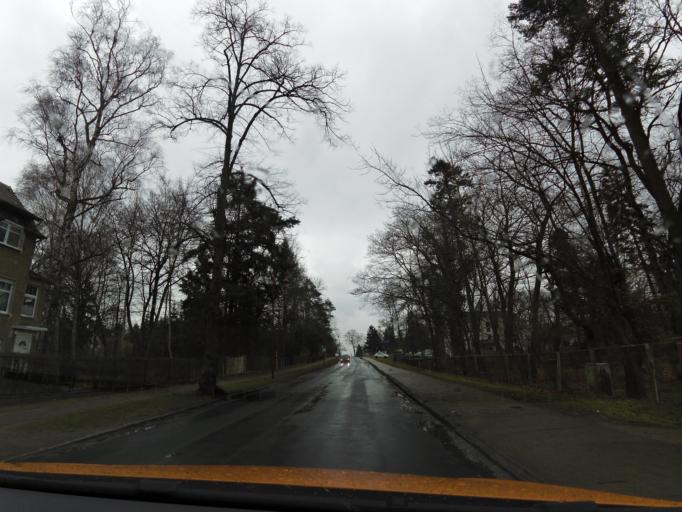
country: DE
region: Brandenburg
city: Rangsdorf
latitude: 52.3284
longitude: 13.4129
